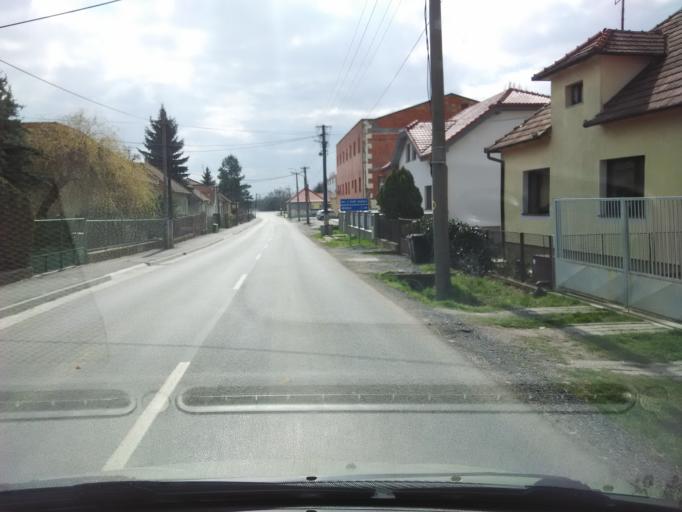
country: SK
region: Nitriansky
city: Zlate Moravce
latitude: 48.3890
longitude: 18.3281
